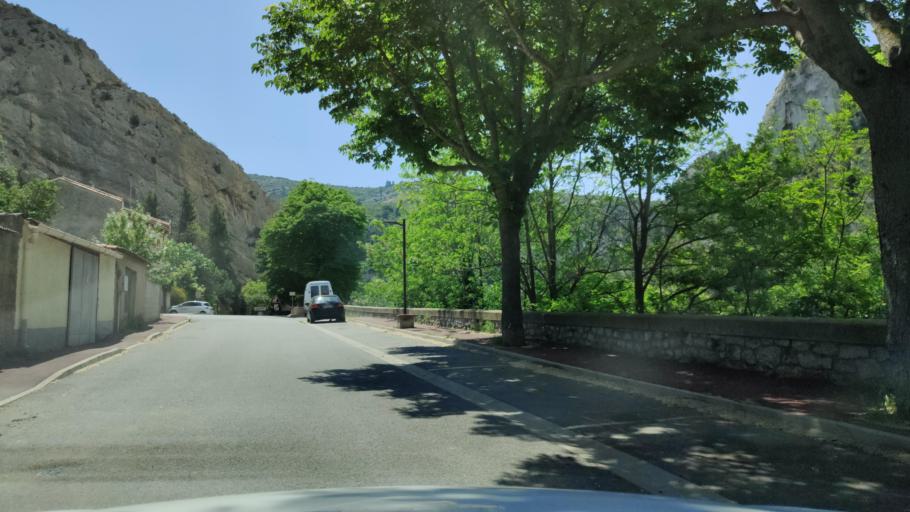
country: FR
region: Languedoc-Roussillon
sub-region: Departement des Pyrenees-Orientales
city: Estagel
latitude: 42.8113
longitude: 2.7442
